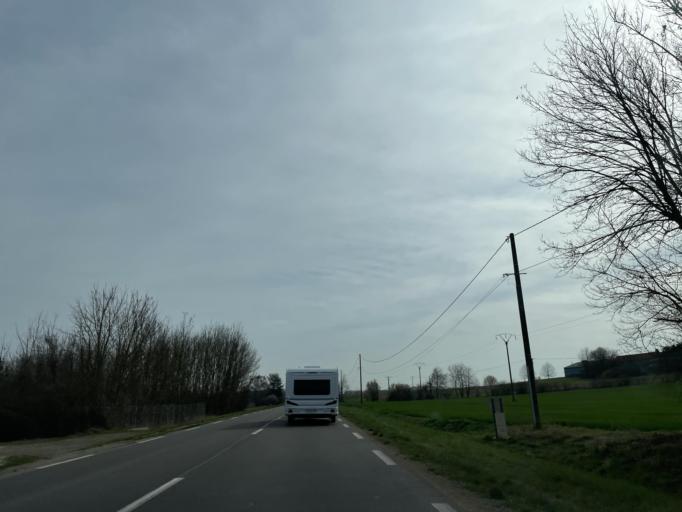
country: FR
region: Champagne-Ardenne
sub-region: Departement de l'Aube
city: Romilly-sur-Seine
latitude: 48.5140
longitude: 3.6703
